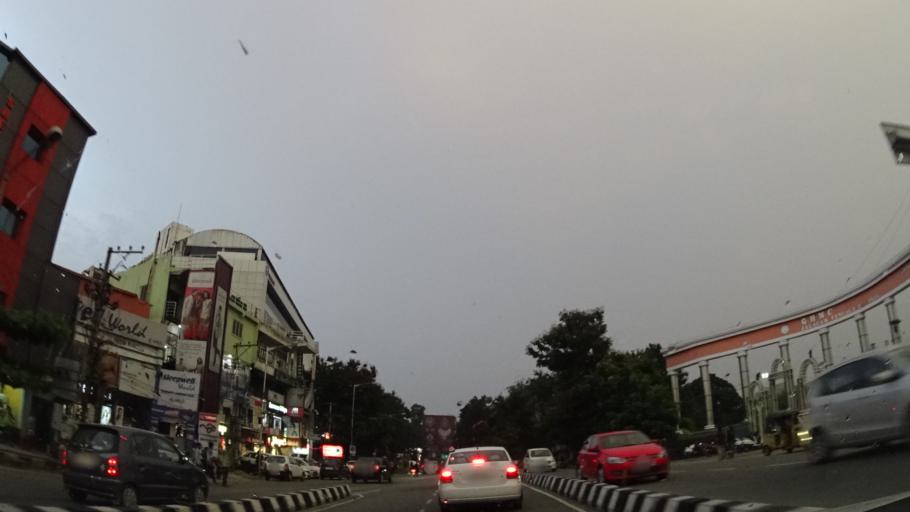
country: IN
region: Telangana
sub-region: Hyderabad
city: Hyderabad
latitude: 17.4237
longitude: 78.4483
